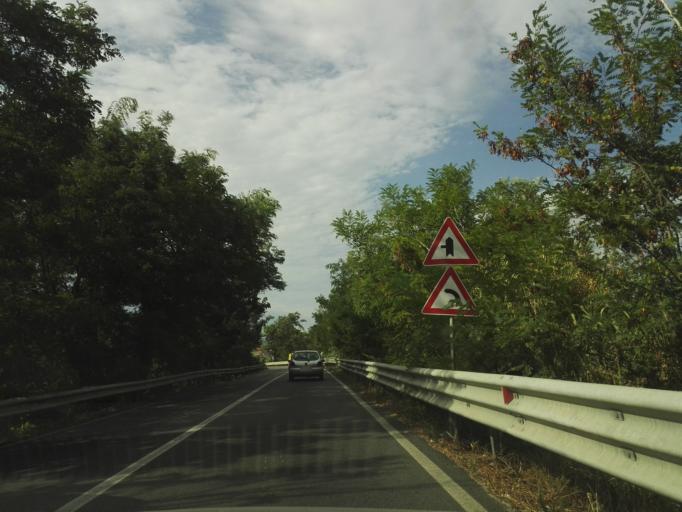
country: IT
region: Calabria
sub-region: Provincia di Catanzaro
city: Marina di Davoli
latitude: 38.6554
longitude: 16.5477
